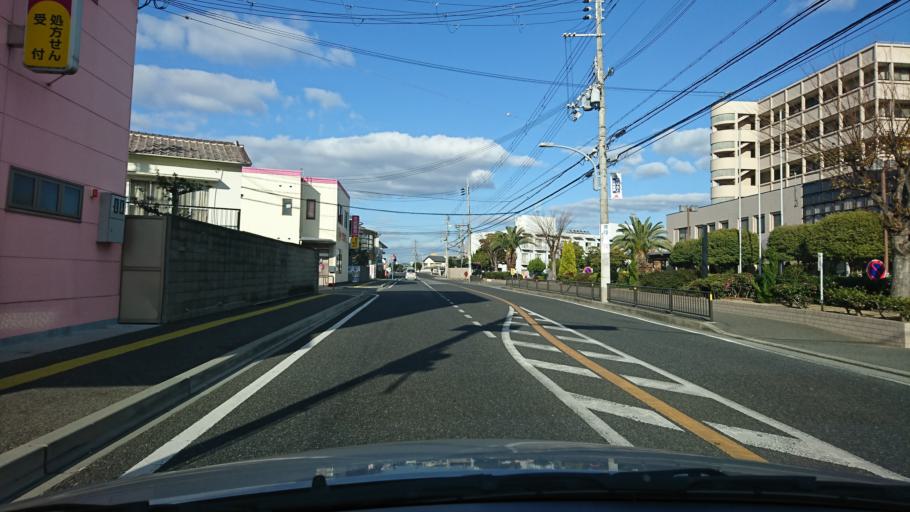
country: JP
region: Hyogo
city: Akashi
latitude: 34.6567
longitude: 134.9893
